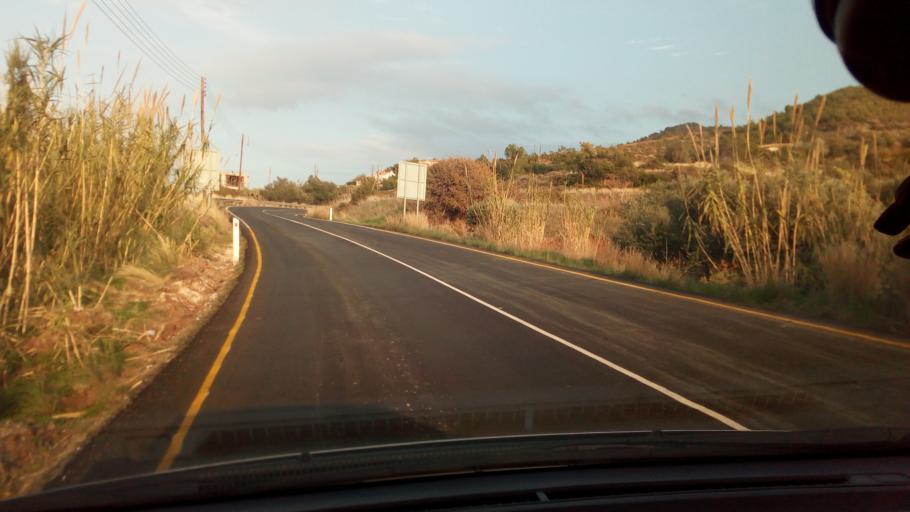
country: CY
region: Pafos
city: Polis
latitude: 35.1426
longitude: 32.5263
